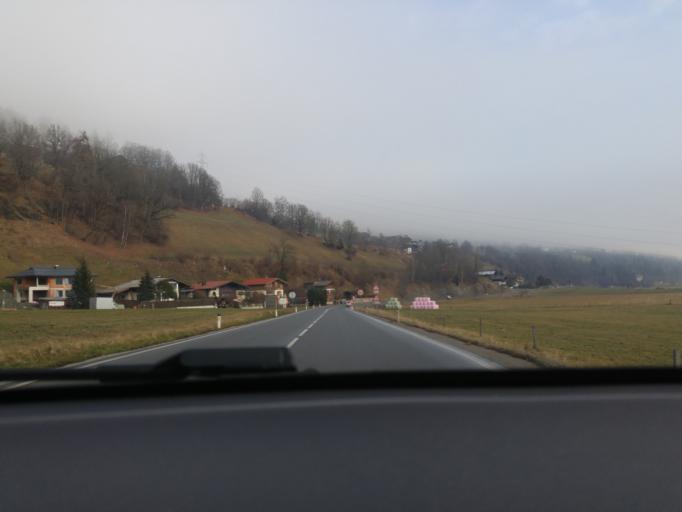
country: AT
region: Salzburg
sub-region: Politischer Bezirk Zell am See
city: Uttendorf
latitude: 47.2843
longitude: 12.5882
